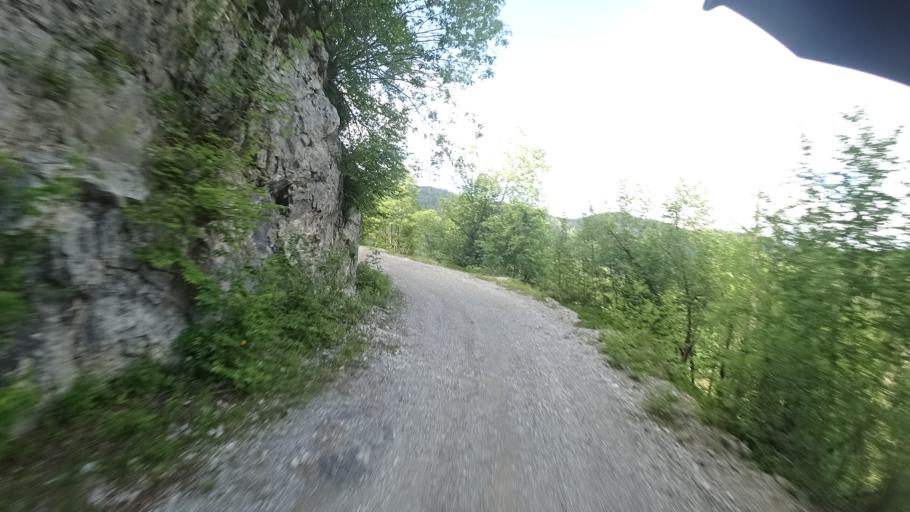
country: SI
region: Osilnica
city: Osilnica
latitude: 45.4682
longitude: 14.7011
